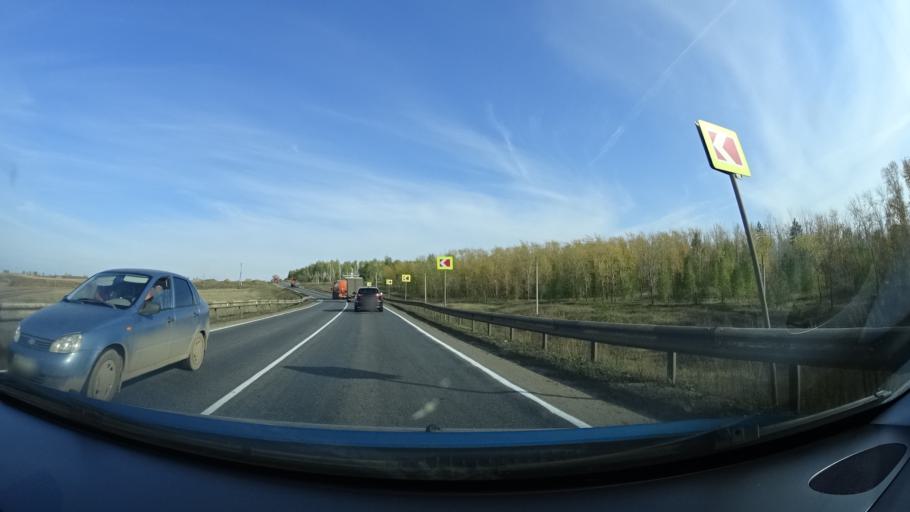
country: RU
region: Bashkortostan
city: Buzdyak
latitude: 54.6597
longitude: 54.6780
